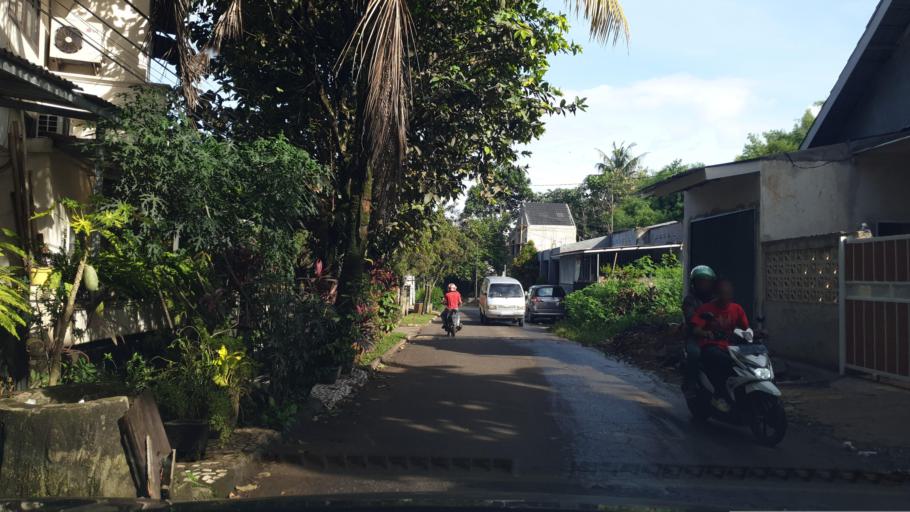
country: ID
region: West Java
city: Sawangan
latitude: -6.3587
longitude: 106.7803
